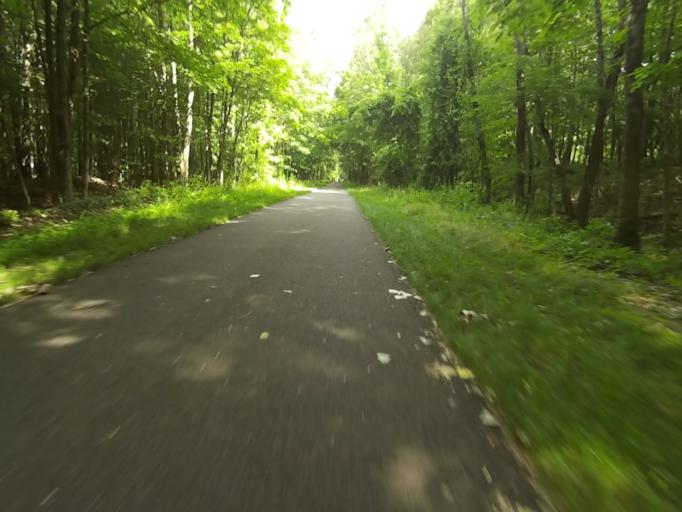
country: US
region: Ohio
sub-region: Summit County
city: Boston Heights
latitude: 41.2661
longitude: -81.5256
